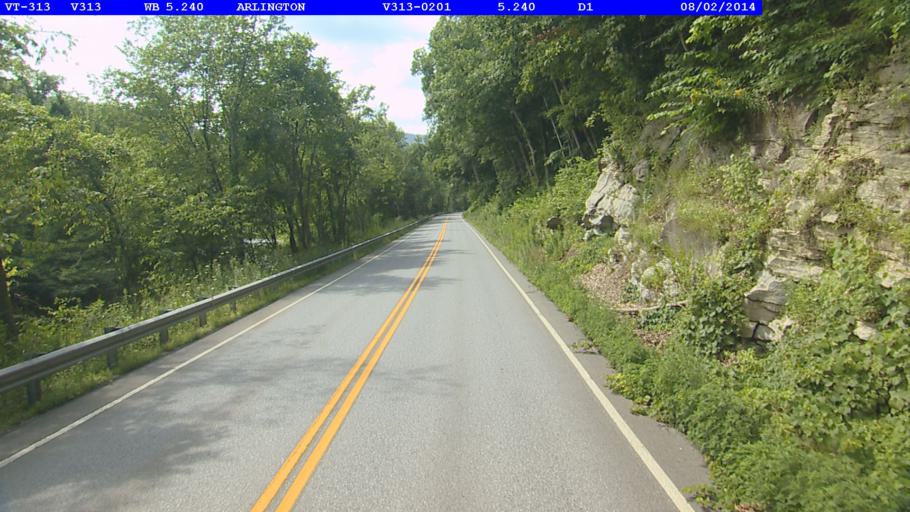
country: US
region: Vermont
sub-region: Bennington County
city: Arlington
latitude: 43.0815
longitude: -73.1782
